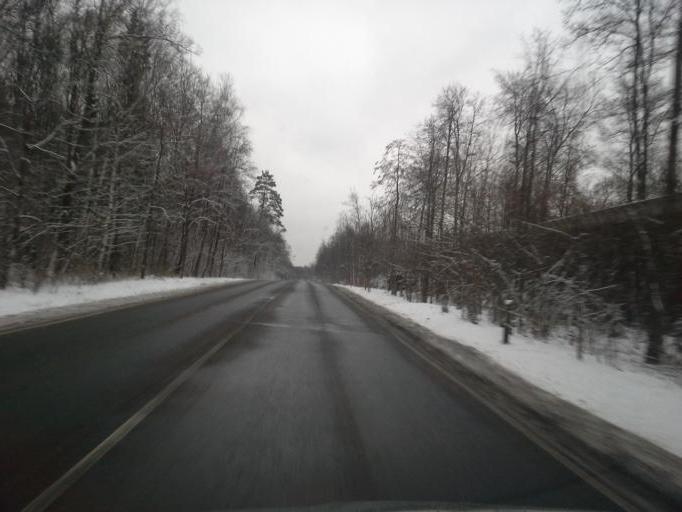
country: RU
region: Moskovskaya
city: Gorki Vtoryye
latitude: 55.6946
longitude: 37.1301
